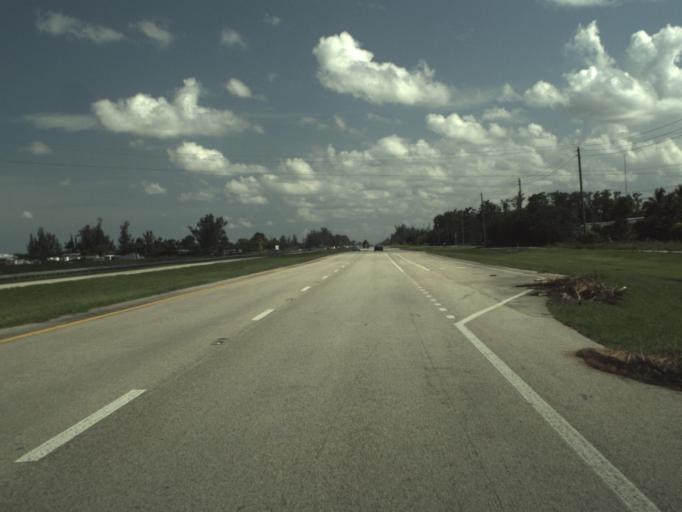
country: US
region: Florida
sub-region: Palm Beach County
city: Villages of Oriole
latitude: 26.4974
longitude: -80.2052
